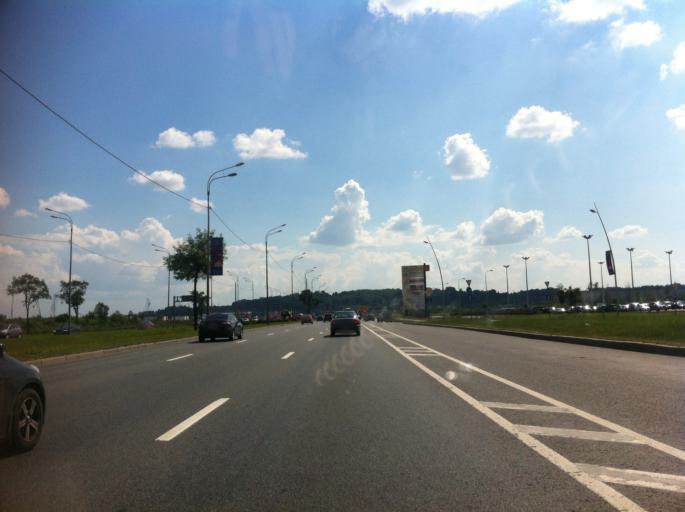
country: RU
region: St.-Petersburg
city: Aleksandrovskaya
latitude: 59.7898
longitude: 30.3245
